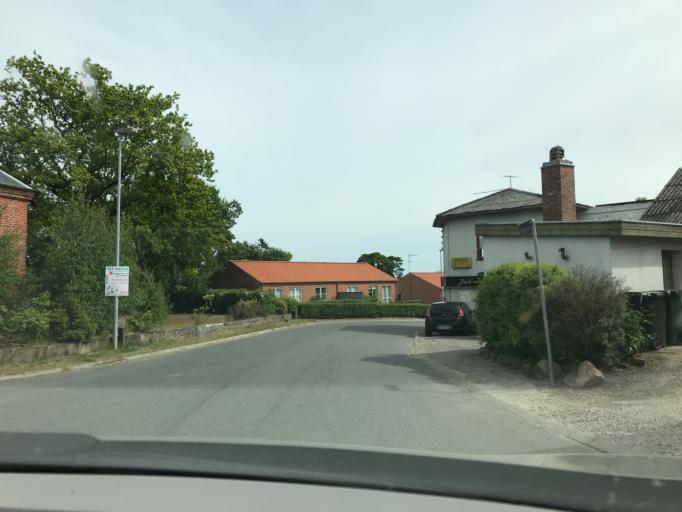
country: DK
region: Central Jutland
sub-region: Norddjurs Kommune
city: Allingabro
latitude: 56.5516
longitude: 10.2990
